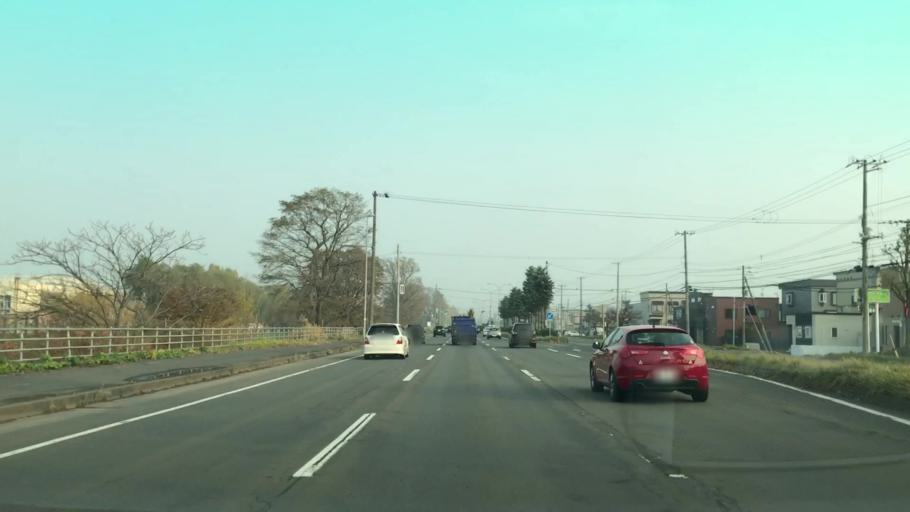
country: JP
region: Hokkaido
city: Sapporo
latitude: 43.1517
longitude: 141.3512
